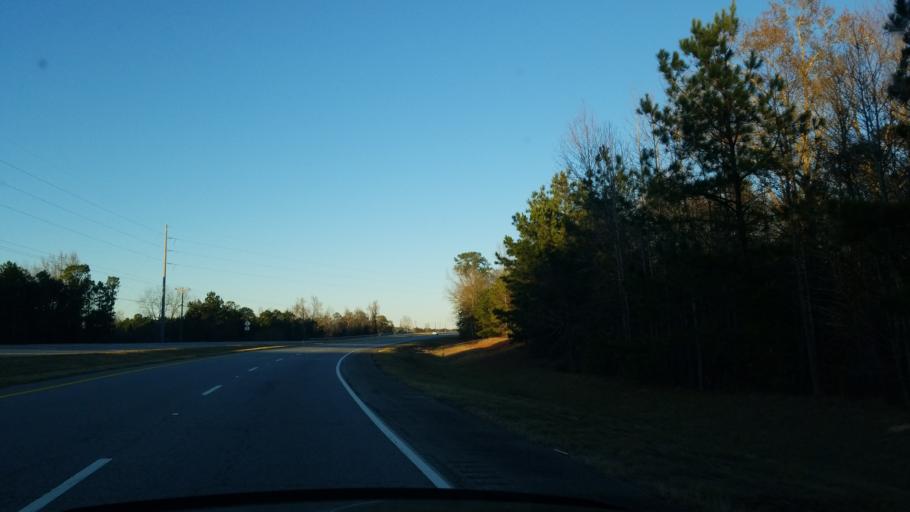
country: US
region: Georgia
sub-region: Chattahoochee County
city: Cusseta
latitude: 32.2802
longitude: -84.7812
